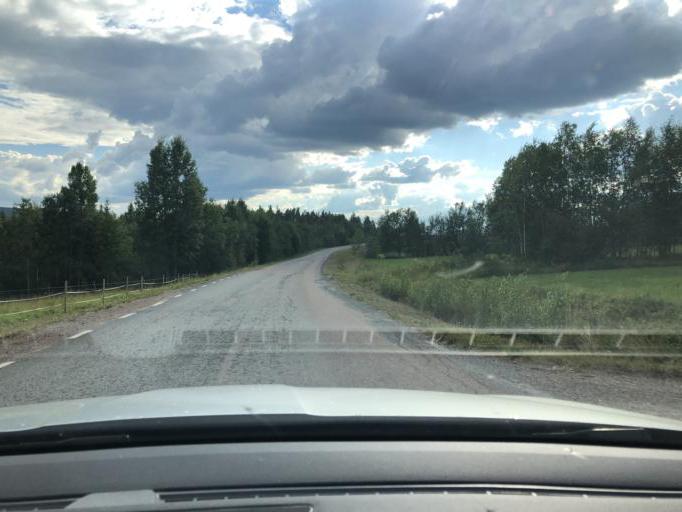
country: SE
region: Vaesternorrland
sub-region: Solleftea Kommun
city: Solleftea
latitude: 63.1959
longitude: 17.0854
